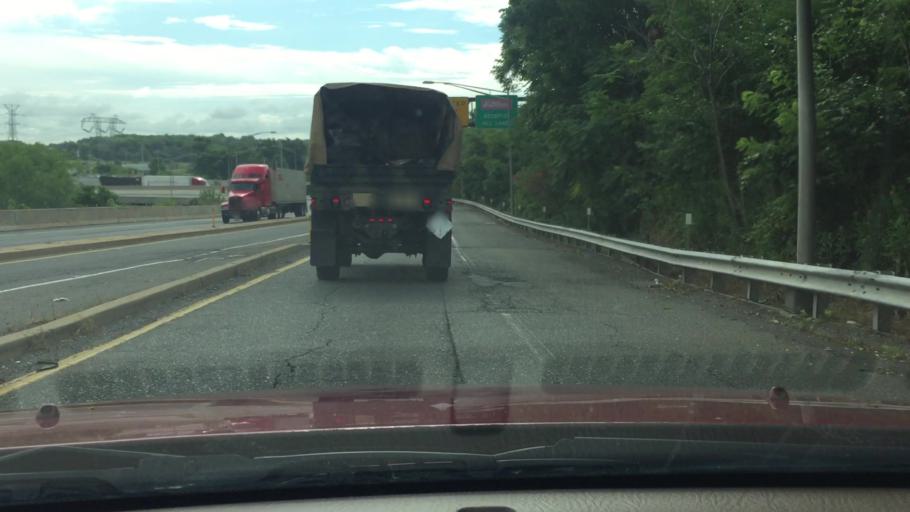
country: US
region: New Jersey
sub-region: Burlington County
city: Bordentown
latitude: 40.1236
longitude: -74.7047
